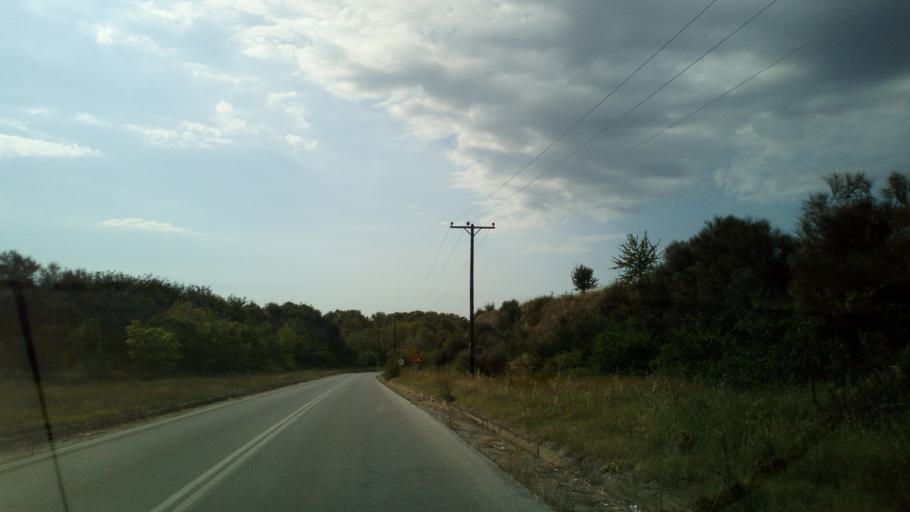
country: GR
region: Central Macedonia
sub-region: Nomos Thessalonikis
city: Gerakarou
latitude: 40.5852
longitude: 23.2558
